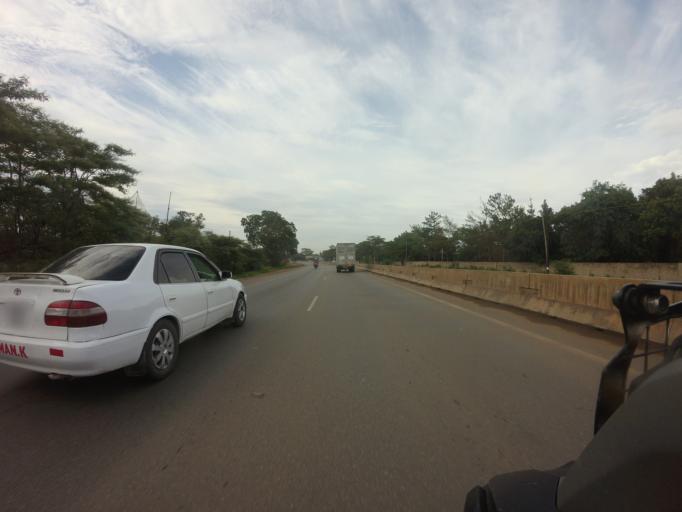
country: ZM
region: Lusaka
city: Lusaka
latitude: -15.5144
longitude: 28.2627
